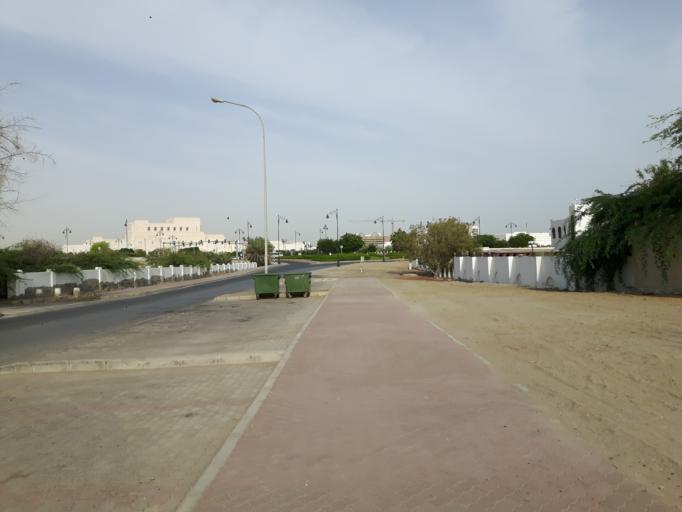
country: OM
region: Muhafazat Masqat
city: Bawshar
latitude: 23.6156
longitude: 58.4732
